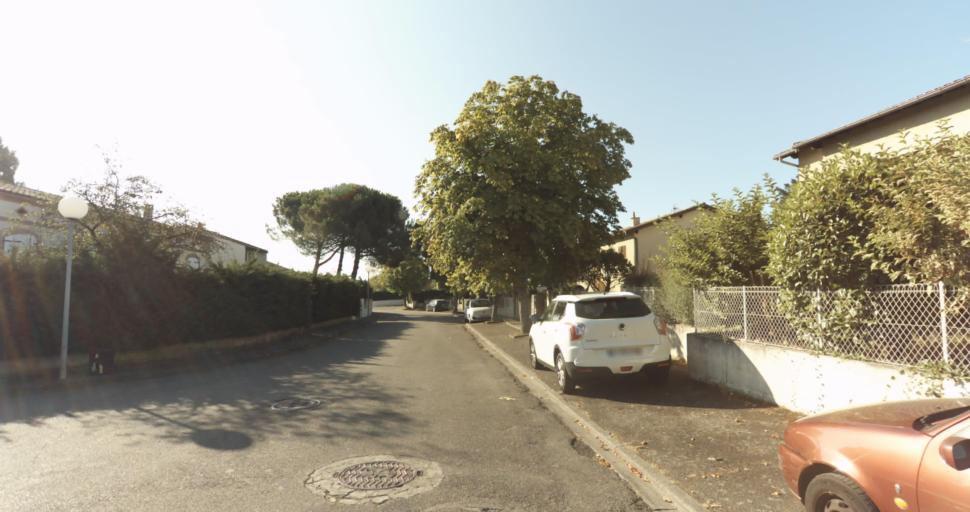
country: FR
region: Midi-Pyrenees
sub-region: Departement de la Haute-Garonne
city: Saint-Jean
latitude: 43.6549
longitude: 1.4943
